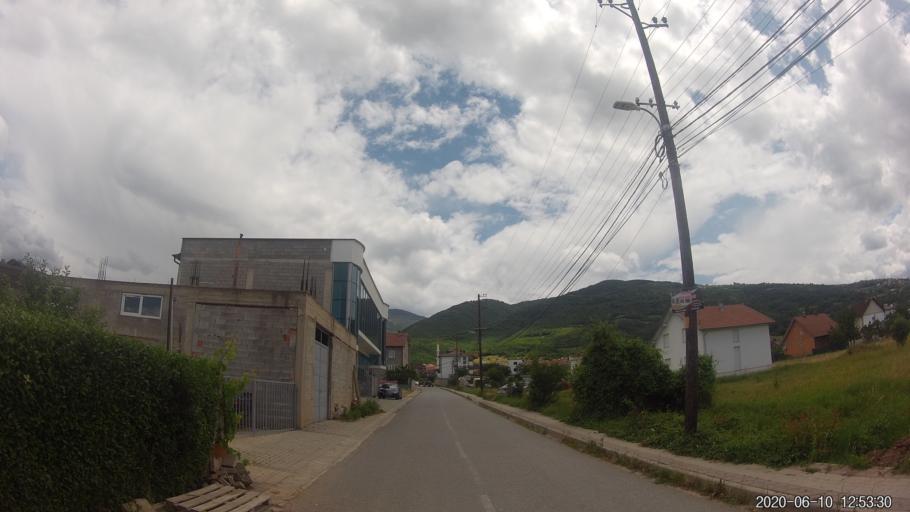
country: XK
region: Prizren
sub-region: Prizren
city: Prizren
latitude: 42.2369
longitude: 20.7660
